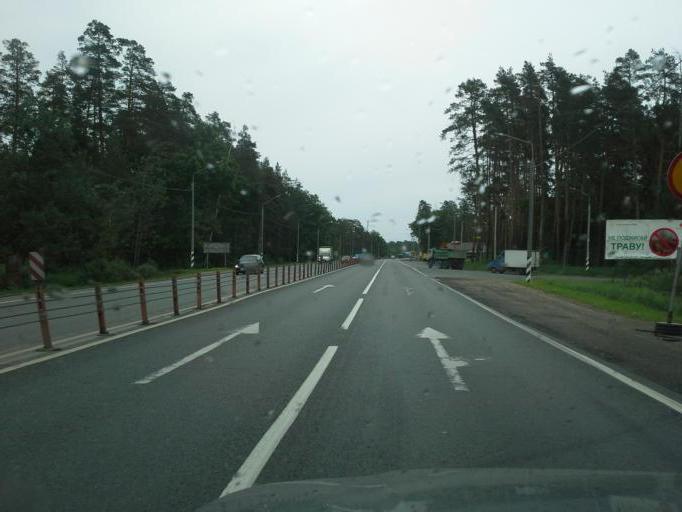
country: RU
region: Moskovskaya
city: Malaya Dubna
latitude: 55.8970
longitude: 39.0470
